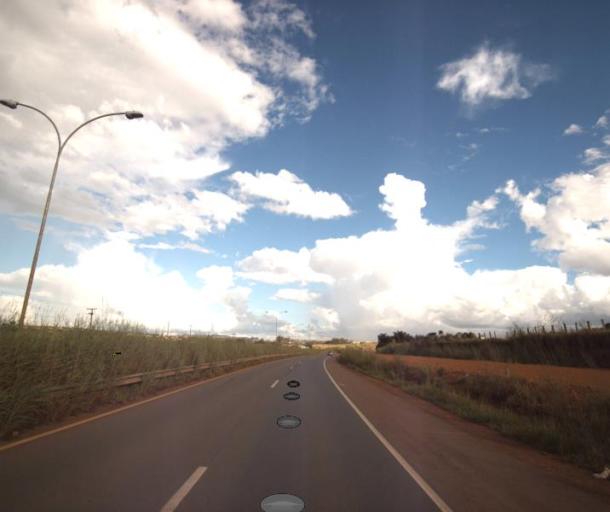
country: BR
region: Goias
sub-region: Anapolis
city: Anapolis
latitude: -16.3009
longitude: -48.9263
